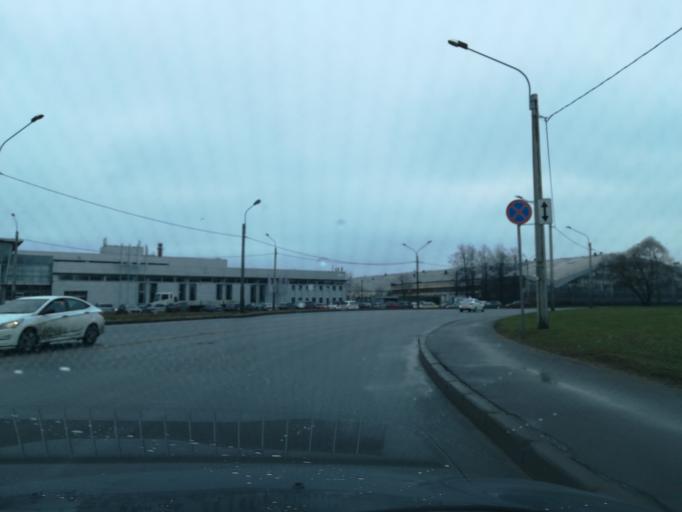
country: RU
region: St.-Petersburg
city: Avtovo
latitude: 59.8618
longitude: 30.2613
